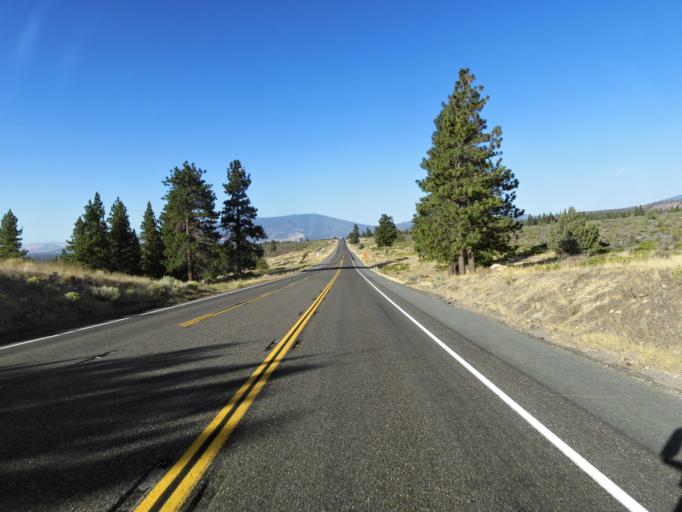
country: US
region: California
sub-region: Siskiyou County
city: Weed
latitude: 41.4854
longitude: -122.3401
